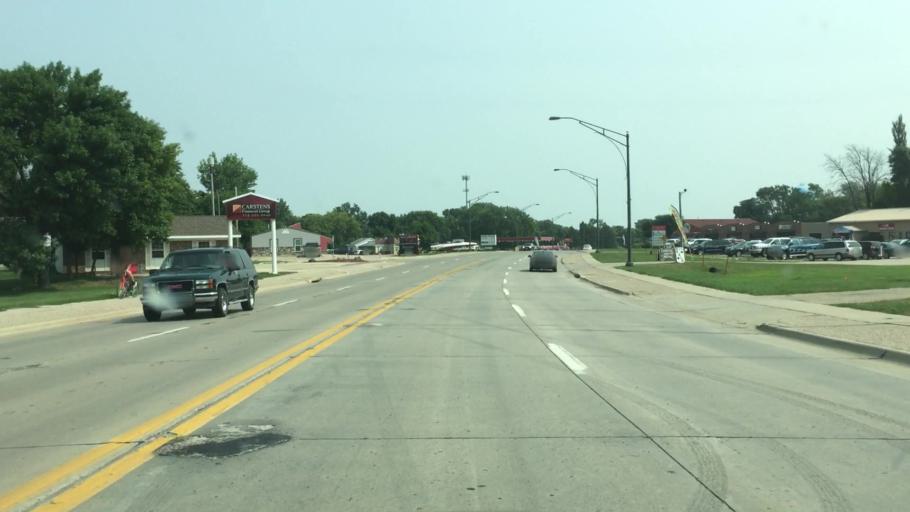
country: US
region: Iowa
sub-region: Dickinson County
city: Arnolds Park
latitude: 43.3608
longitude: -95.1409
